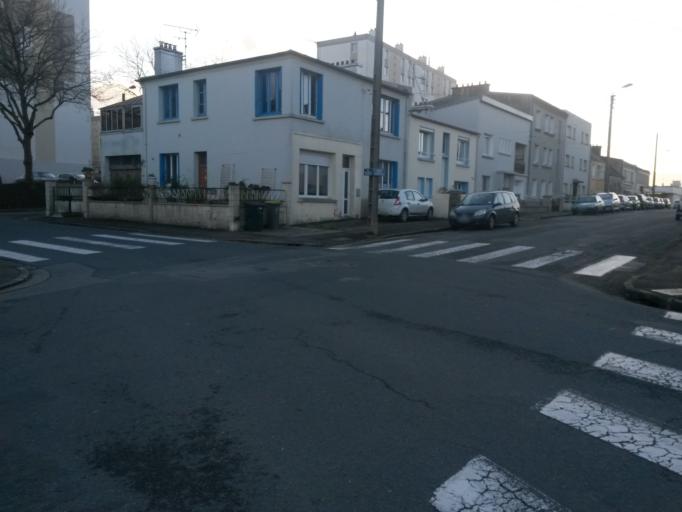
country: FR
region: Brittany
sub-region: Departement du Finistere
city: Brest
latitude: 48.3972
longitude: -4.4614
